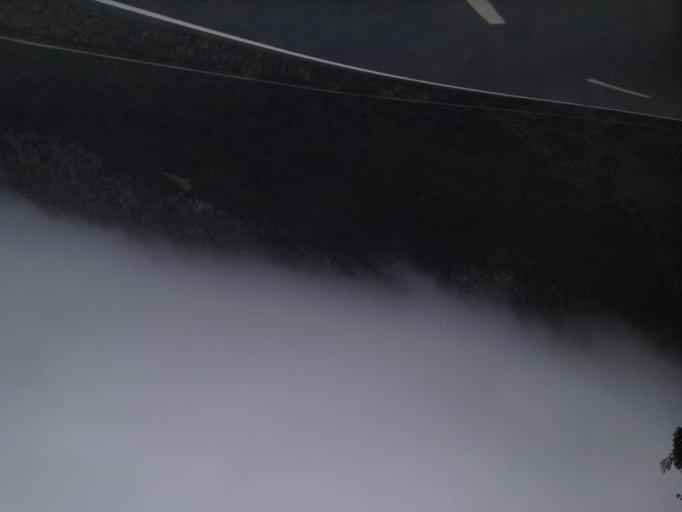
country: ES
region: Balearic Islands
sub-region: Illes Balears
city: Fornalutx
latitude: 39.7980
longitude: 2.7729
